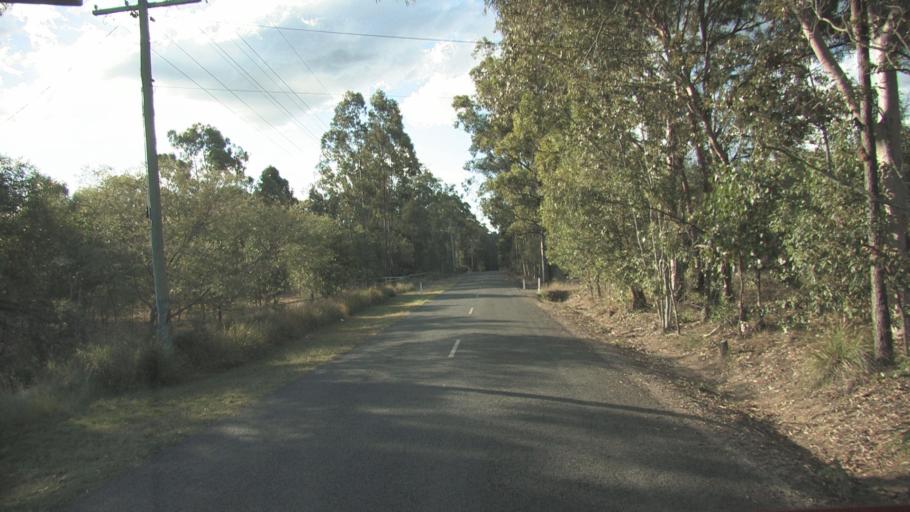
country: AU
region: Queensland
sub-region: Ipswich
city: Springfield Lakes
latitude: -27.6949
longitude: 152.9539
